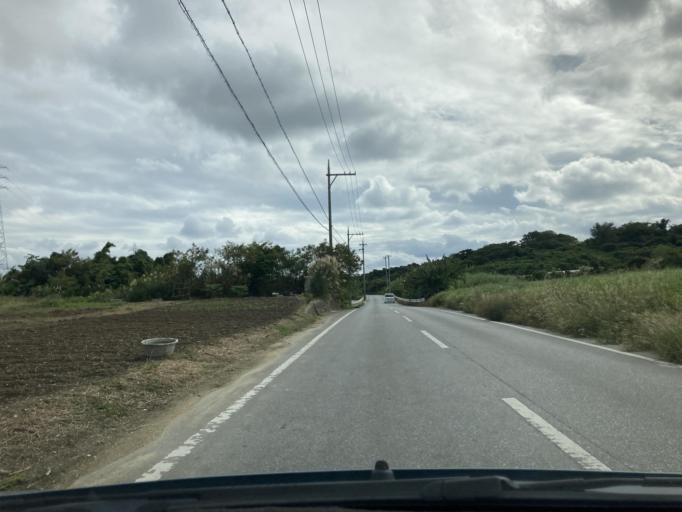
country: JP
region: Okinawa
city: Itoman
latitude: 26.1173
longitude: 127.6878
